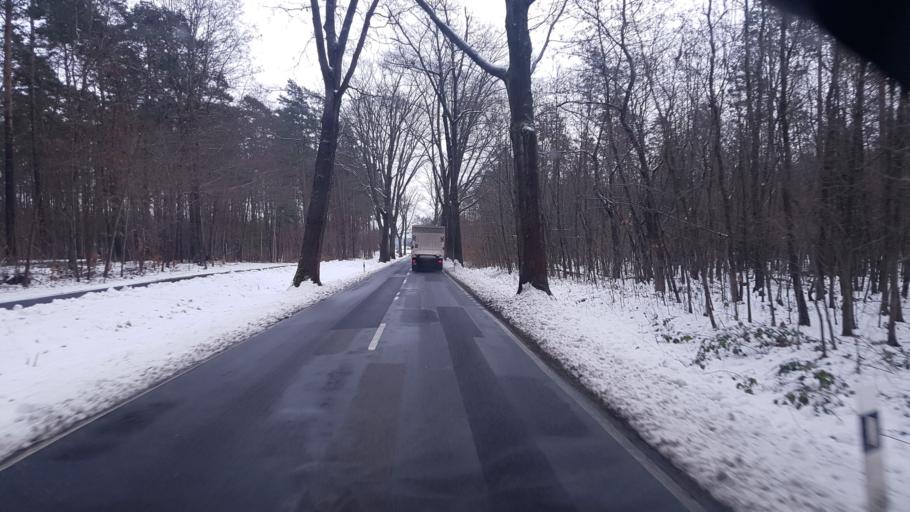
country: DE
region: Brandenburg
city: Lawitz
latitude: 52.0808
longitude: 14.5288
